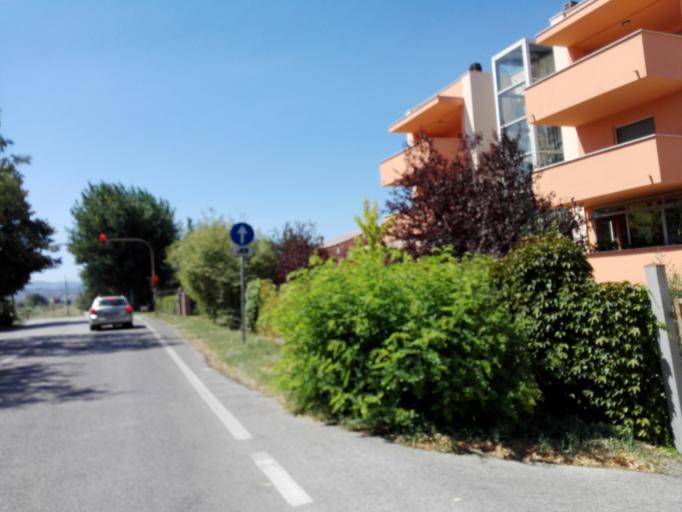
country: IT
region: Umbria
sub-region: Provincia di Perugia
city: Foligno
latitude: 42.9505
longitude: 12.6921
